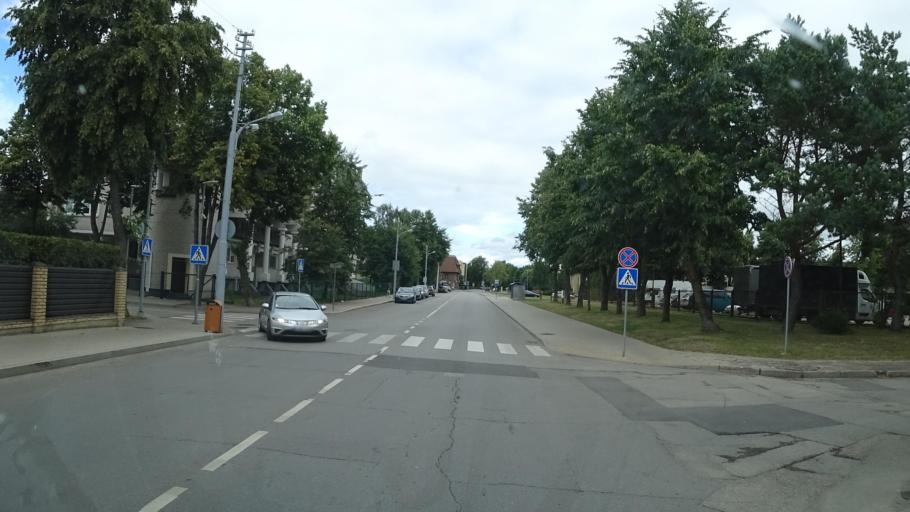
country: LT
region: Klaipedos apskritis
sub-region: Klaipeda
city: Palanga
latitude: 55.9237
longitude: 21.0748
